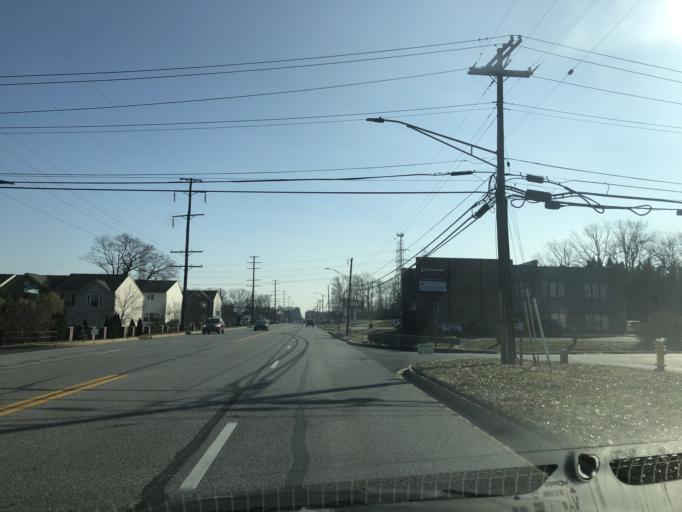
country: US
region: Maryland
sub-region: Anne Arundel County
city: Odenton
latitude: 39.0843
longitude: -76.6940
